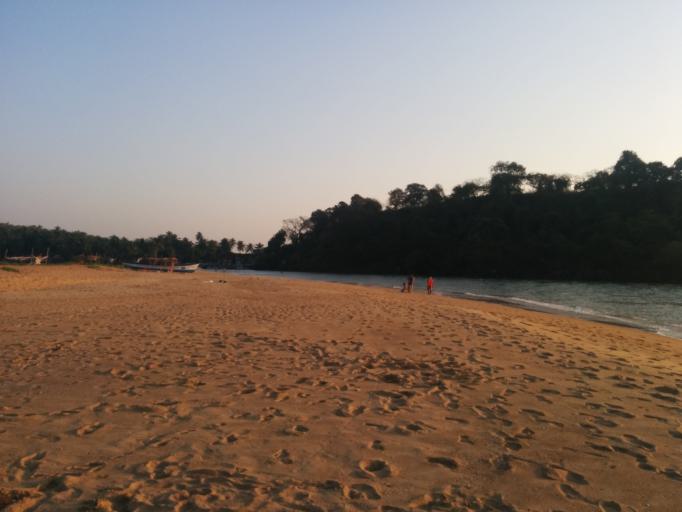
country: IN
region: Karnataka
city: Canacona
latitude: 14.9859
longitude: 74.0383
